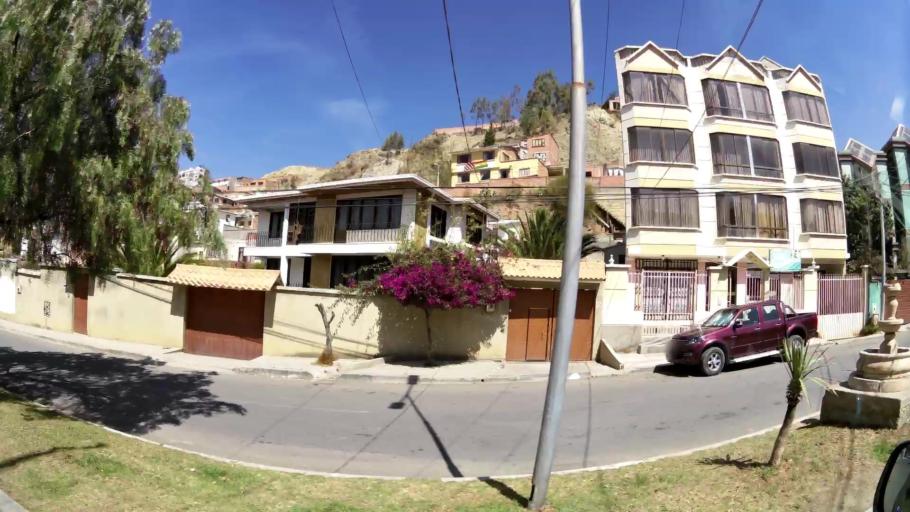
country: BO
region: La Paz
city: La Paz
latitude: -16.5447
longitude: -68.0966
